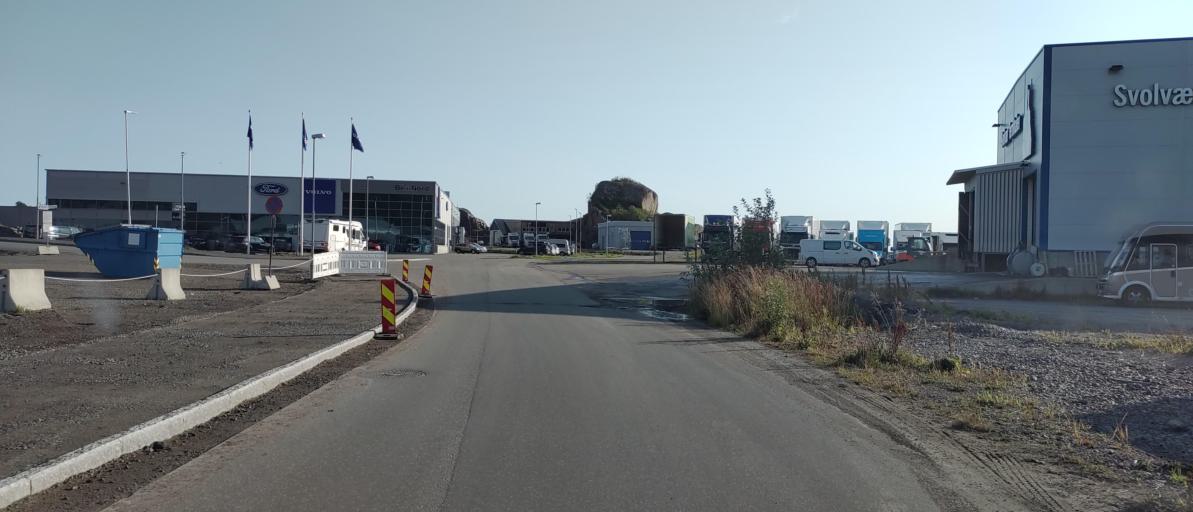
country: NO
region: Nordland
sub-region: Vagan
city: Svolvaer
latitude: 68.2275
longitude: 14.5557
